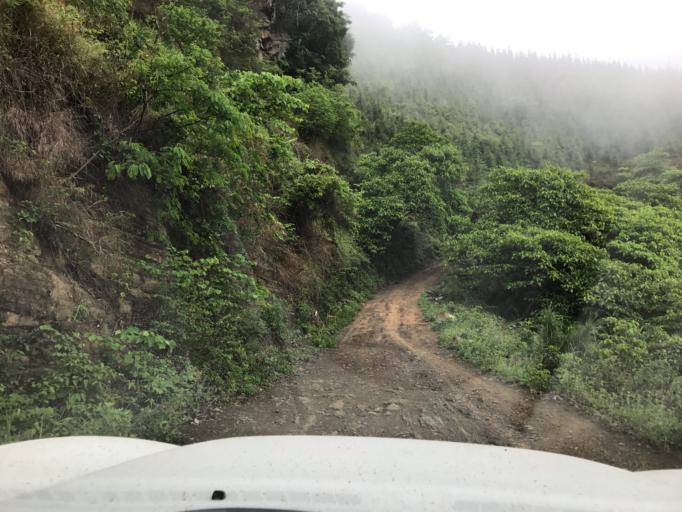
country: CN
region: Guangxi Zhuangzu Zizhiqu
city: Leli
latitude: 24.8061
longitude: 106.0775
